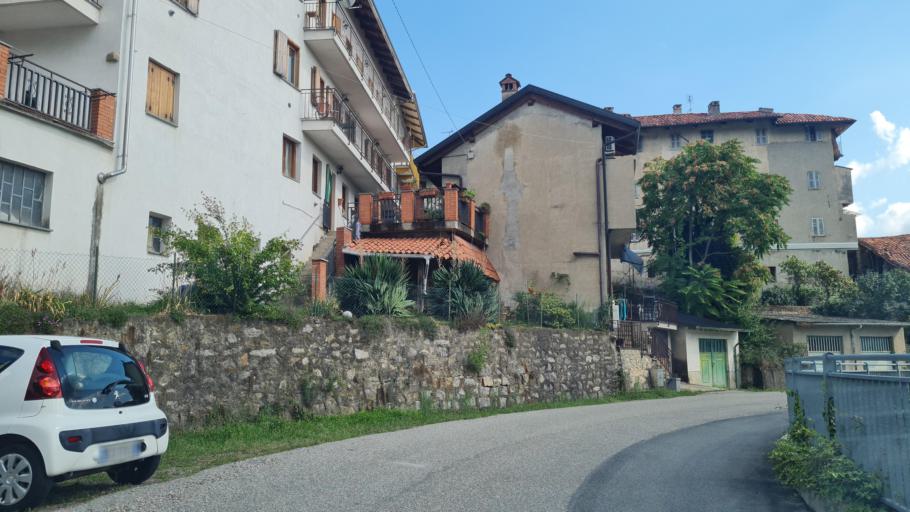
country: IT
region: Piedmont
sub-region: Provincia di Biella
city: Fontanella-Ozino
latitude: 45.6157
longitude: 8.1706
